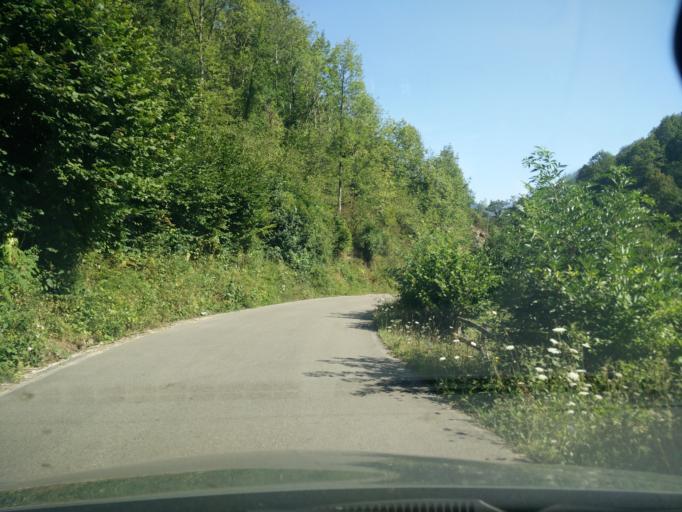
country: ES
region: Asturias
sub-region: Province of Asturias
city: Campo de Caso
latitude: 43.1714
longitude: -5.3925
